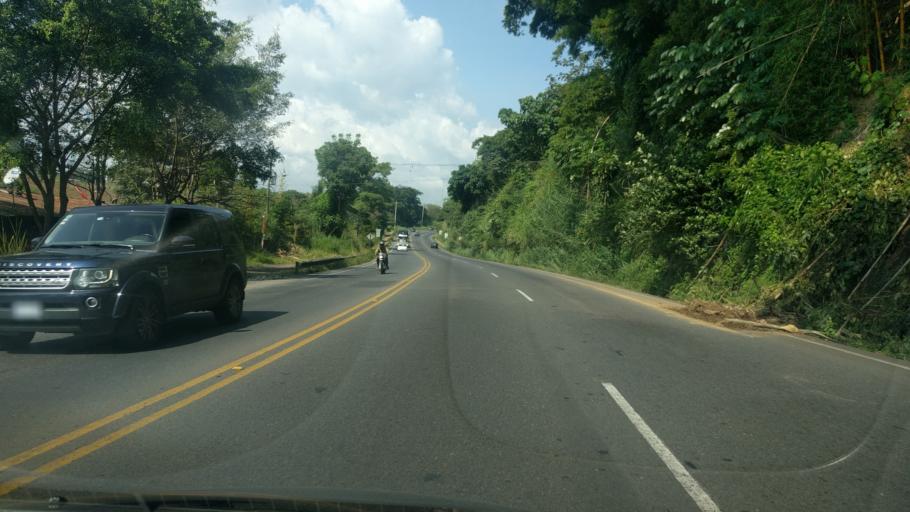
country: CR
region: Alajuela
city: Carrillos
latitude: 10.0035
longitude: -84.3001
